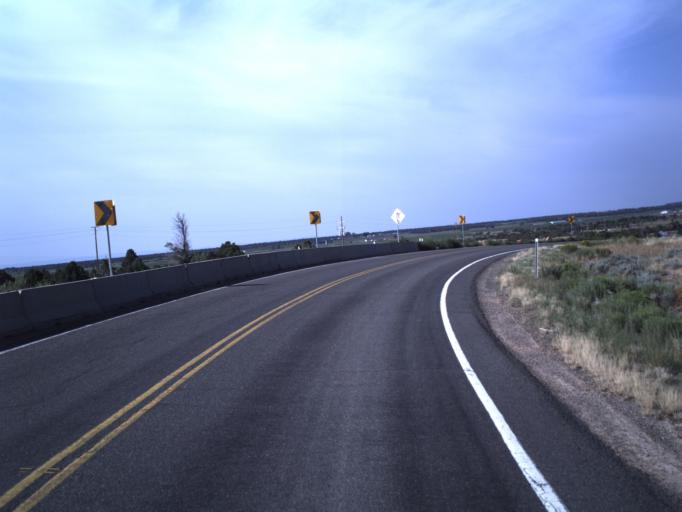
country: US
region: Utah
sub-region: Duchesne County
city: Duchesne
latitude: 40.3535
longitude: -110.3949
